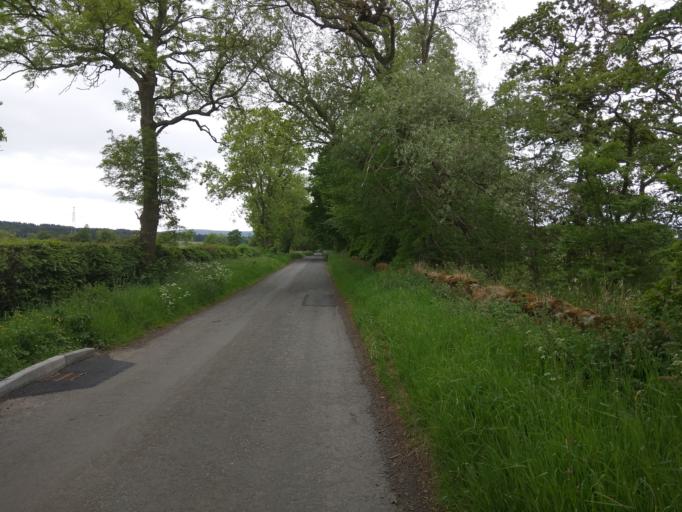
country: GB
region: Scotland
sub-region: Edinburgh
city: Balerno
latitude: 55.8726
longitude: -3.3591
